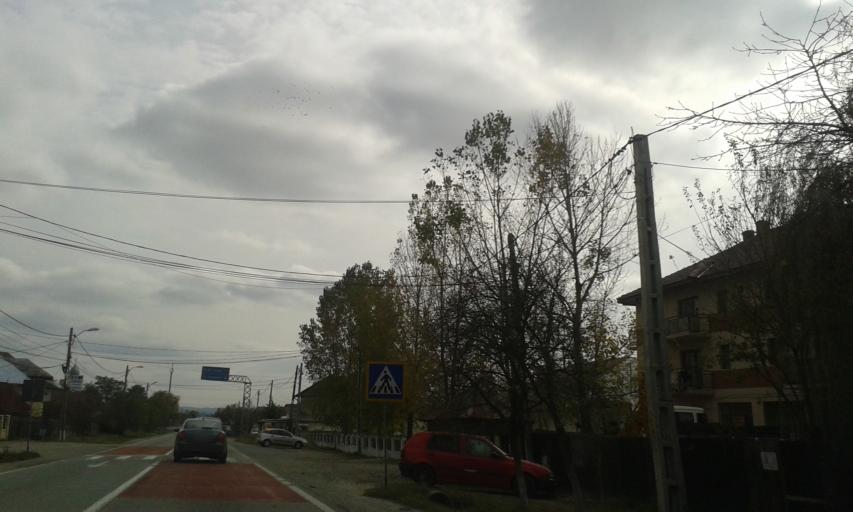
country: RO
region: Gorj
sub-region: Comuna Scoarta
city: Scoarta
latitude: 45.0185
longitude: 23.4645
